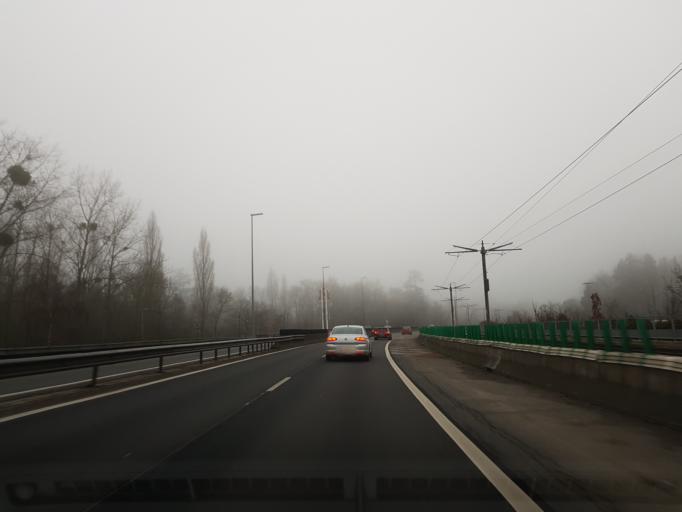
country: FR
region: Centre
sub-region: Departement du Loiret
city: Olivet
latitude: 47.8665
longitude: 1.9128
